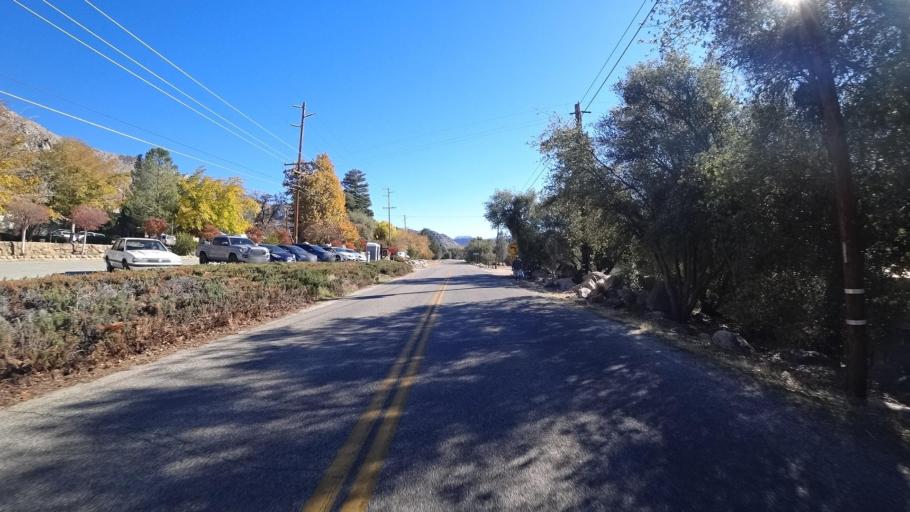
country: US
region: California
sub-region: Kern County
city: Kernville
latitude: 35.7695
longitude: -118.4297
